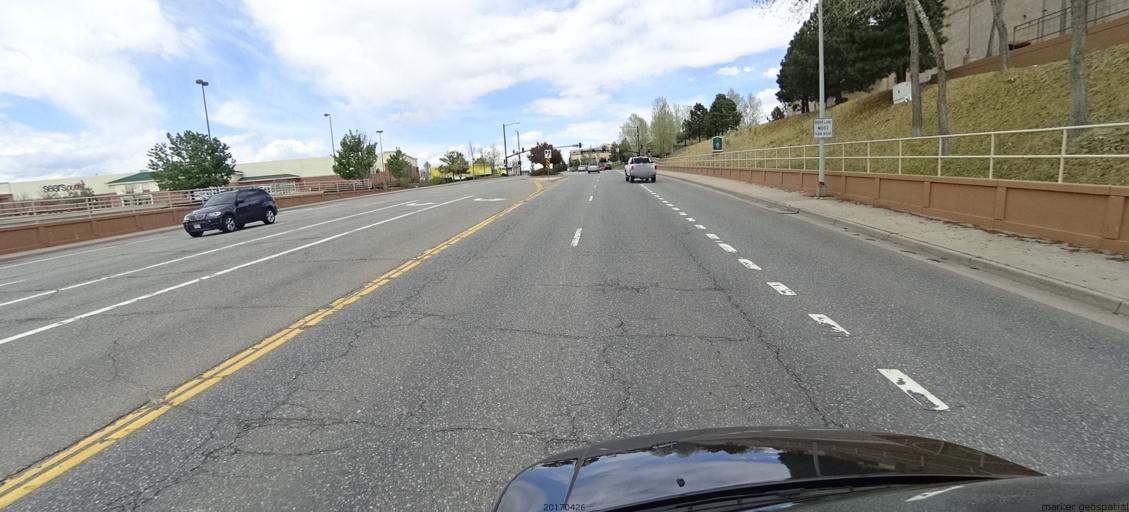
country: US
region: Colorado
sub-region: Adams County
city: Lone Tree
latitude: 39.5593
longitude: -104.8805
